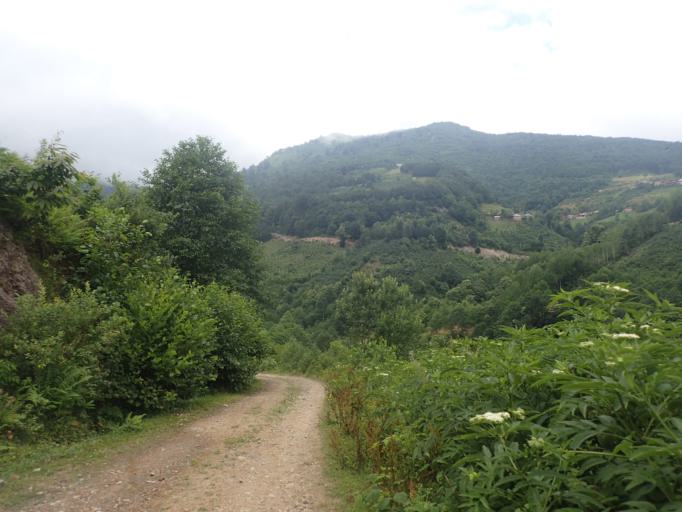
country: TR
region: Ordu
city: Akkus
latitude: 40.8641
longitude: 37.0082
